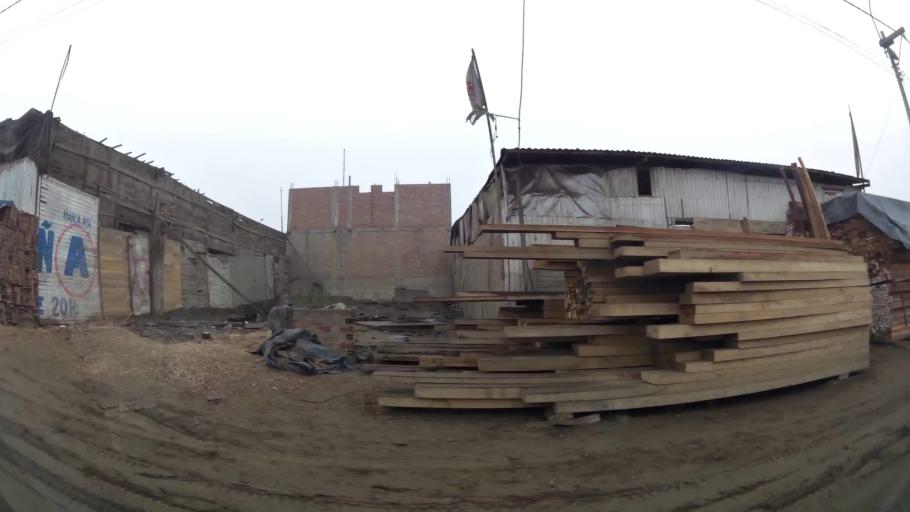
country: PE
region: Lima
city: Ventanilla
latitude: -11.8365
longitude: -77.1400
